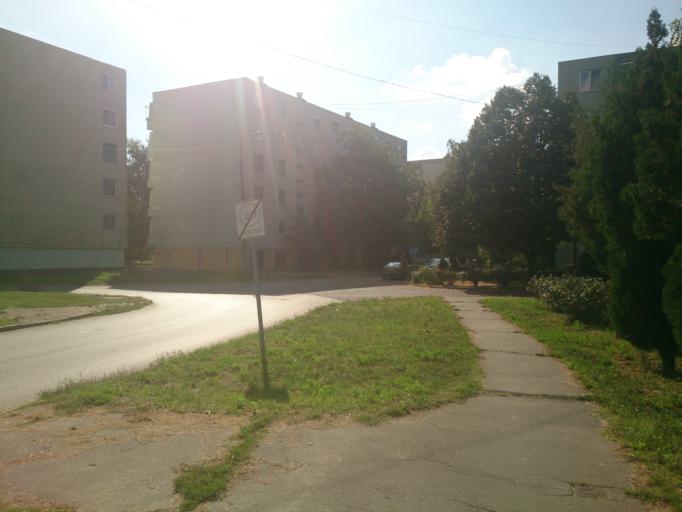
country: HU
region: Csongrad
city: Szeged
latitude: 46.2773
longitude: 20.1541
